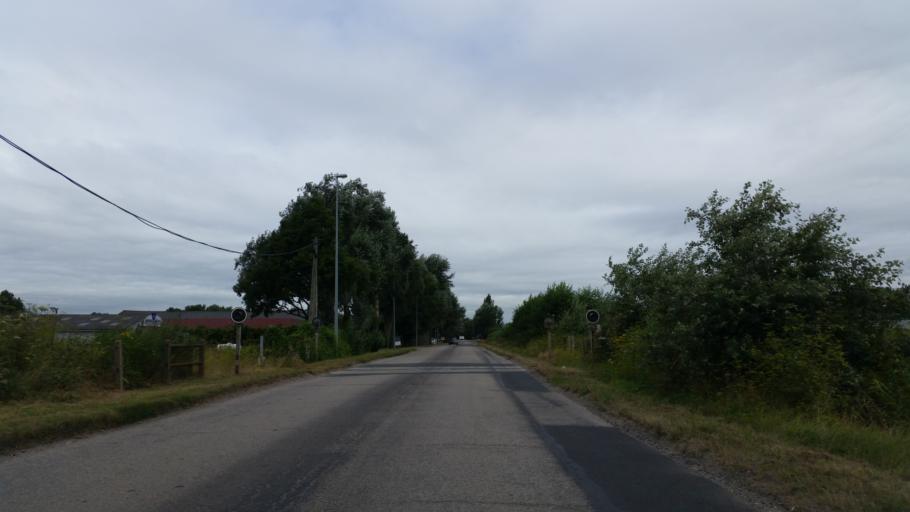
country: FR
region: Lower Normandy
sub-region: Departement du Calvados
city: La Riviere-Saint-Sauveur
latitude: 49.4208
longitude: 0.2600
